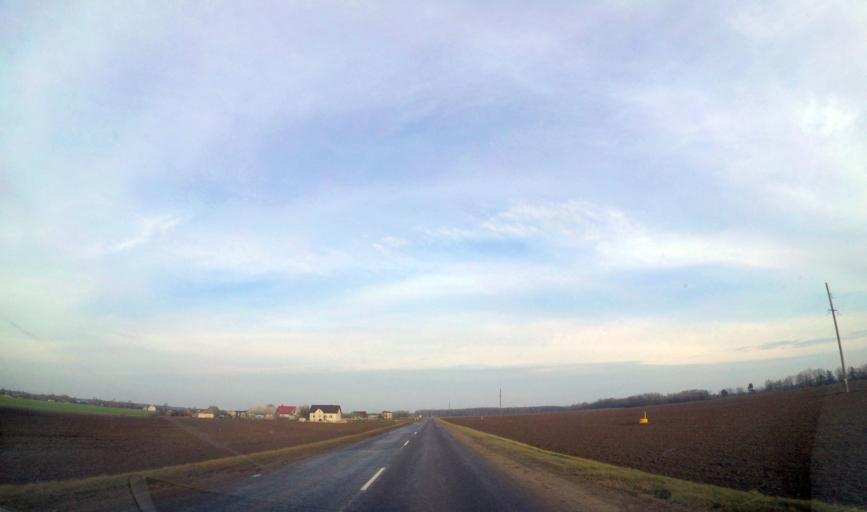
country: BY
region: Grodnenskaya
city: Hrodna
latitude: 53.7426
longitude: 23.9336
